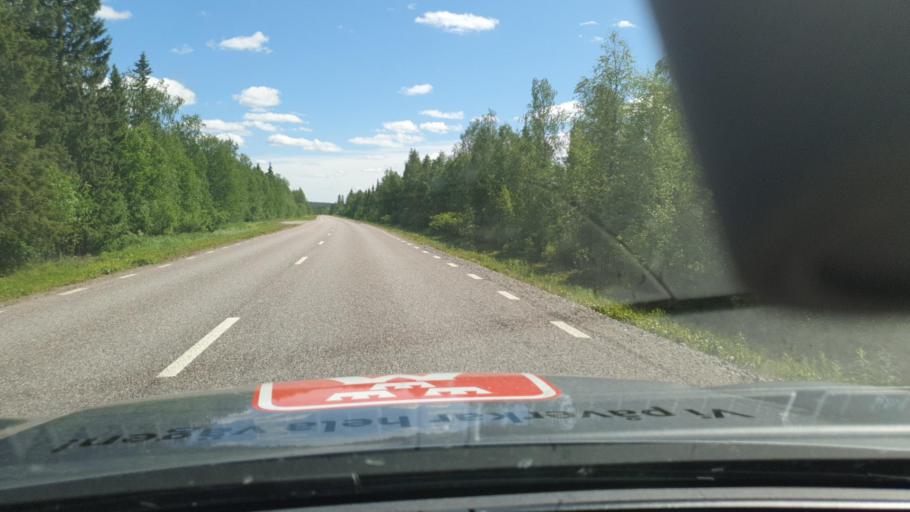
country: SE
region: Norrbotten
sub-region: Pajala Kommun
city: Pajala
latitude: 67.1148
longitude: 23.6167
